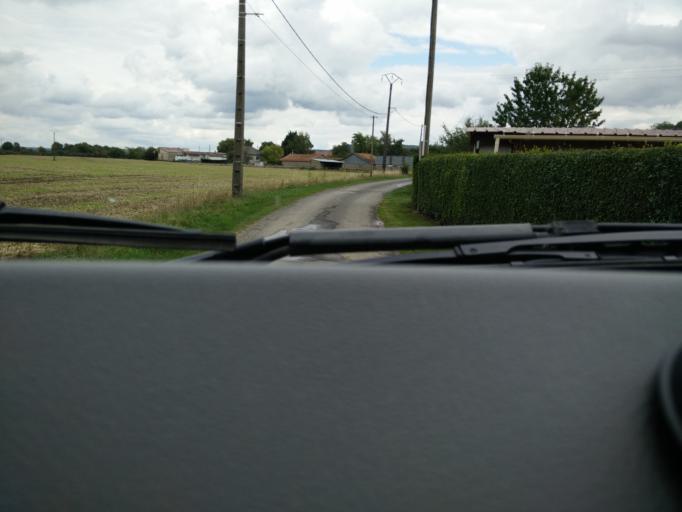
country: FR
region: Lorraine
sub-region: Departement de la Meuse
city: Stenay
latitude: 49.3899
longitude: 5.1798
